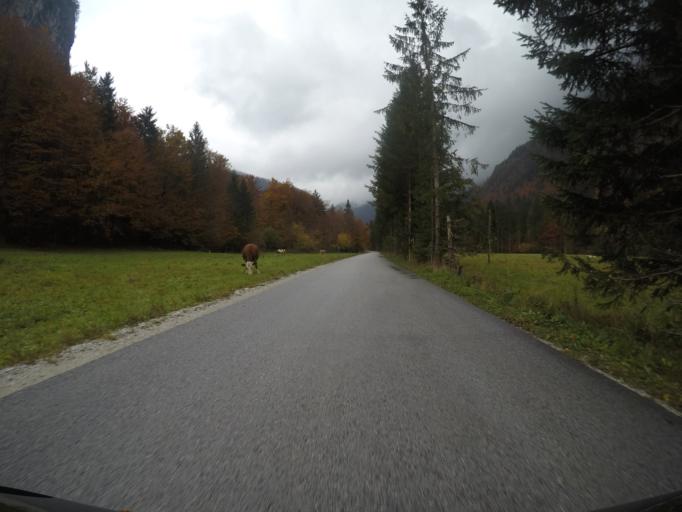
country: SI
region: Jesenice
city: Hrusica
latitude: 46.4109
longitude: 13.9958
